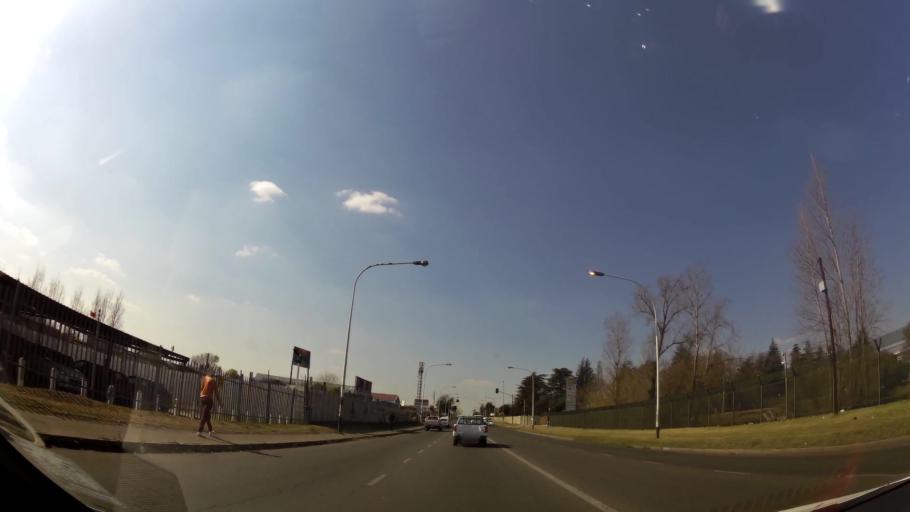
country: ZA
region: Gauteng
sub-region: Ekurhuleni Metropolitan Municipality
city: Boksburg
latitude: -26.2087
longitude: 28.2717
